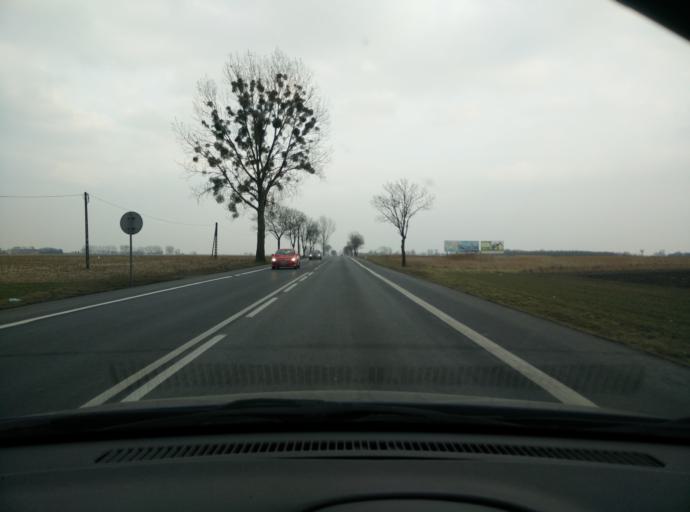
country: PL
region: Greater Poland Voivodeship
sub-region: Powiat poznanski
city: Kornik
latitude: 52.2450
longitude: 17.1219
